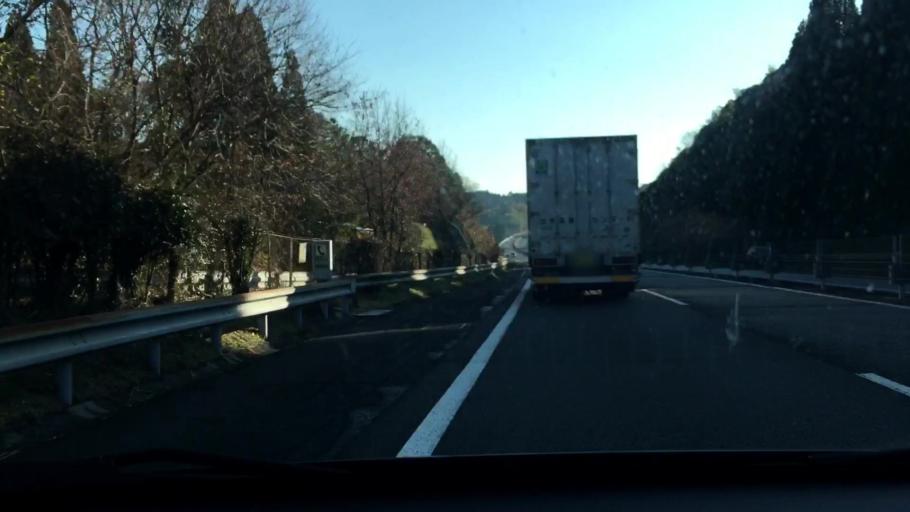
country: JP
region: Kagoshima
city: Kajiki
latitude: 31.8843
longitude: 130.6956
